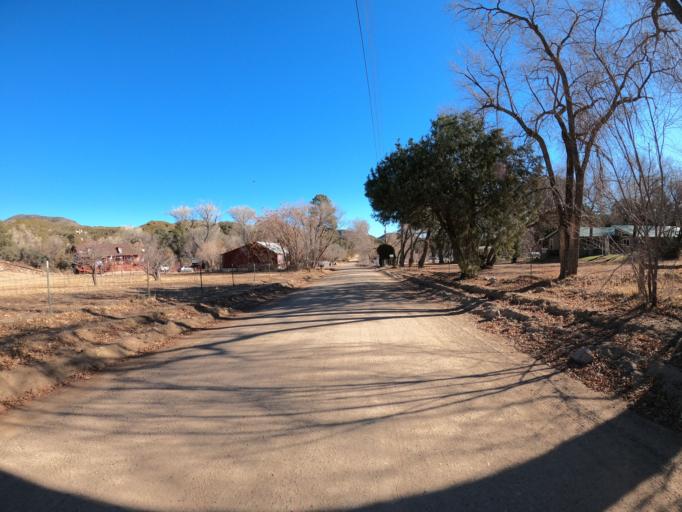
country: US
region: Arizona
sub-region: Yavapai County
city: Verde Village
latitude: 34.5880
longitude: -112.0465
